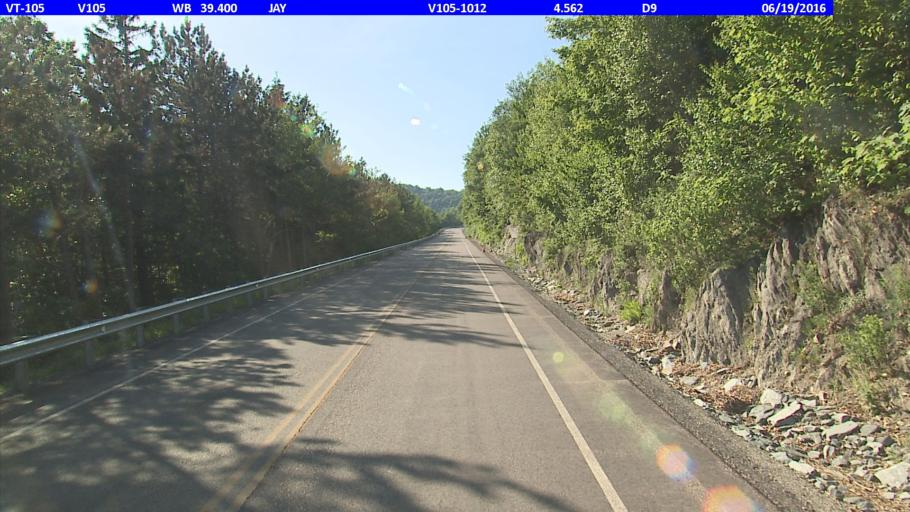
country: CA
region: Quebec
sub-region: Monteregie
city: Sutton
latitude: 44.9838
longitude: -72.4921
